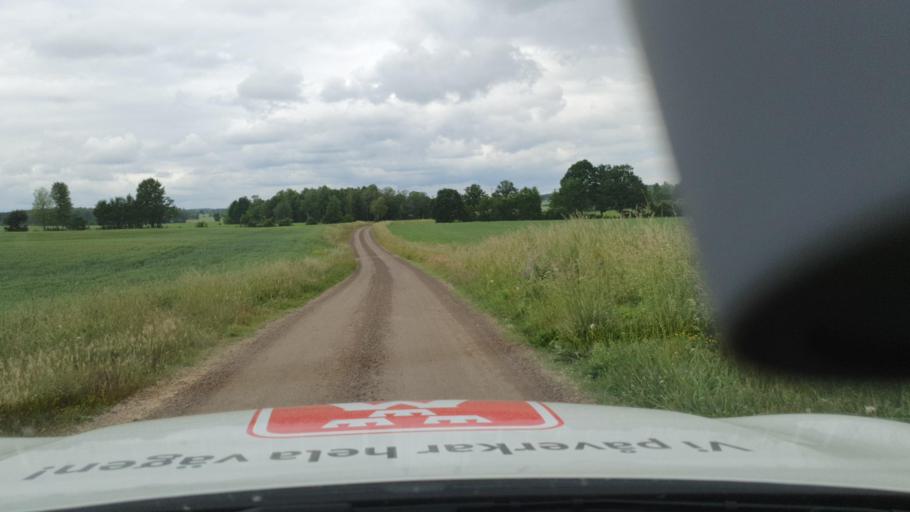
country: SE
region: Vaestra Goetaland
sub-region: Hjo Kommun
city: Hjo
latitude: 58.1809
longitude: 14.1729
